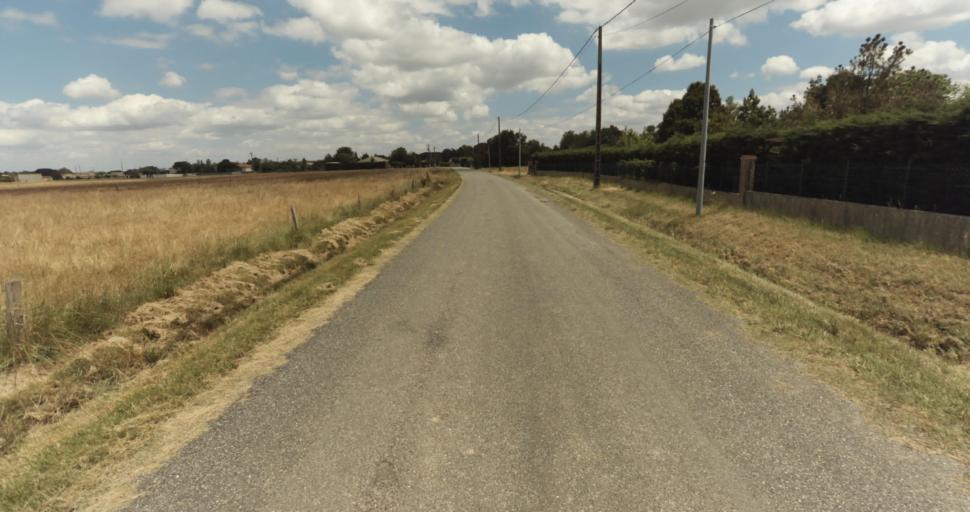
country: FR
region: Midi-Pyrenees
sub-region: Departement de la Haute-Garonne
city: Fontenilles
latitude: 43.5410
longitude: 1.1793
